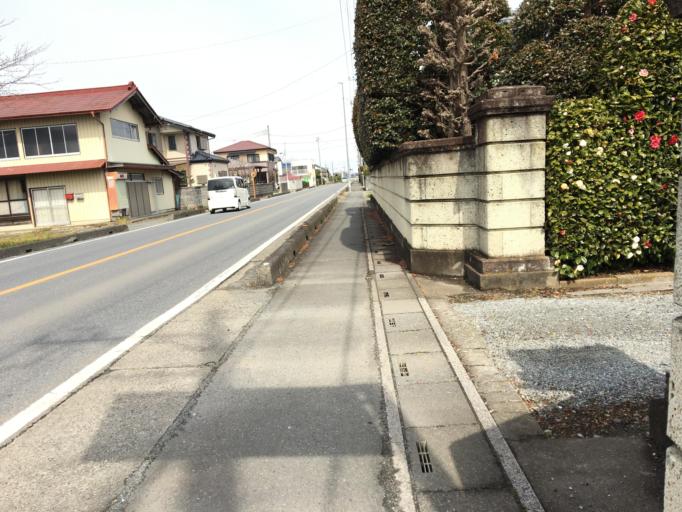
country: JP
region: Saitama
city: Yorii
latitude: 36.1366
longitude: 139.2133
